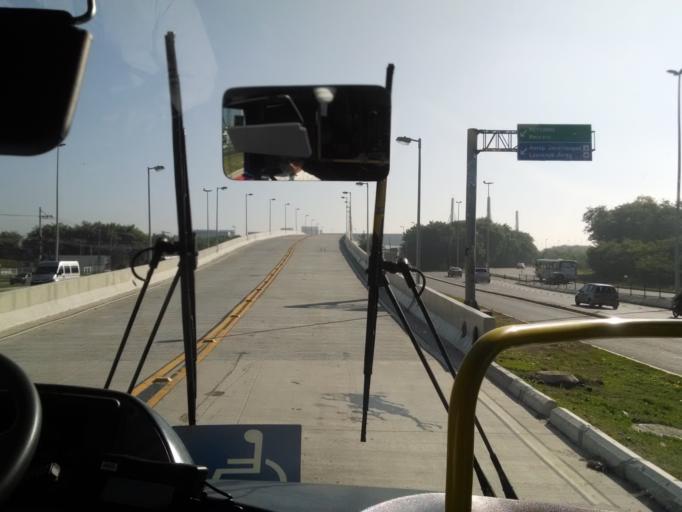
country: BR
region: Rio de Janeiro
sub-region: Rio De Janeiro
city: Rio de Janeiro
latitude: -22.9807
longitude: -43.3656
